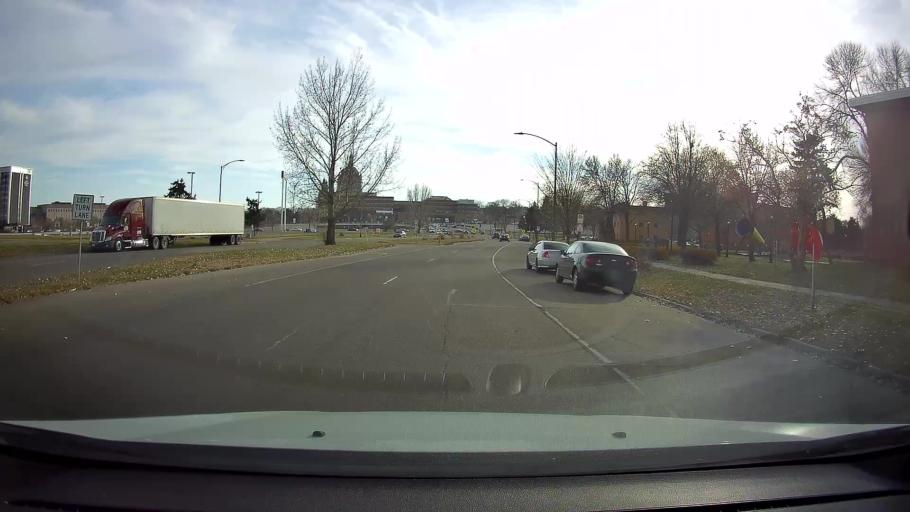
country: US
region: Minnesota
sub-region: Ramsey County
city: Saint Paul
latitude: 44.9536
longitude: -93.1096
